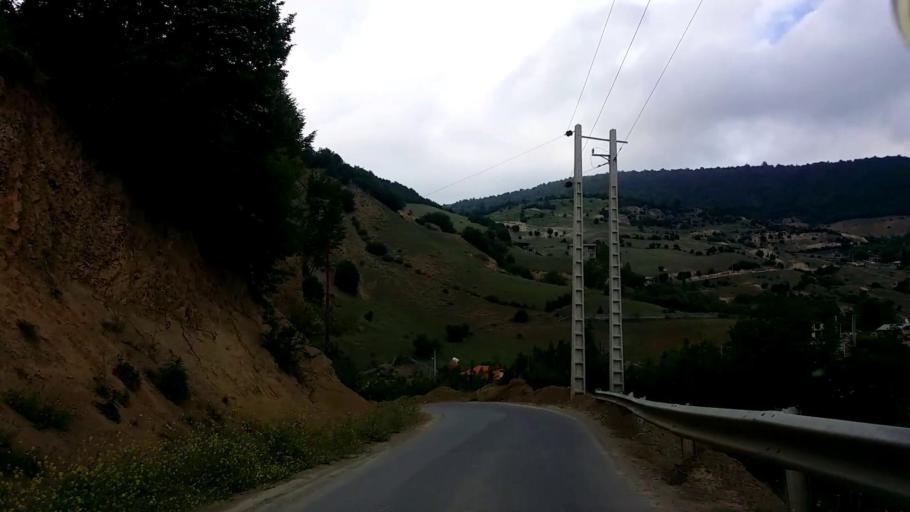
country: IR
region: Mazandaran
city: Chalus
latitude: 36.5516
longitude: 51.2700
